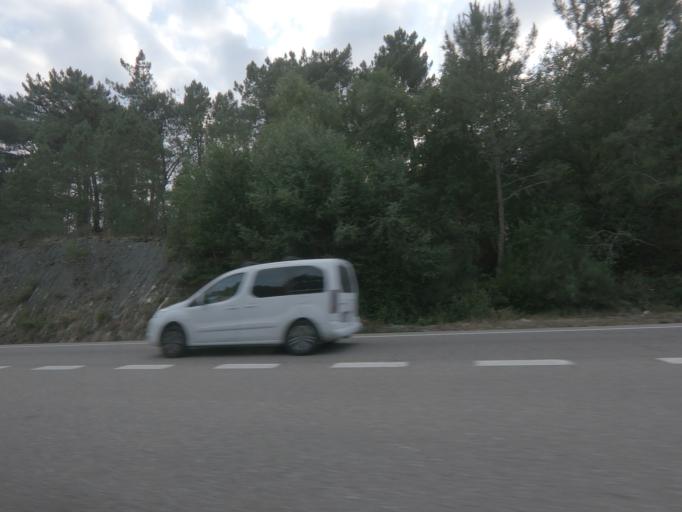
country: ES
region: Galicia
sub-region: Provincia de Ourense
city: Taboadela
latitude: 42.2297
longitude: -7.8428
